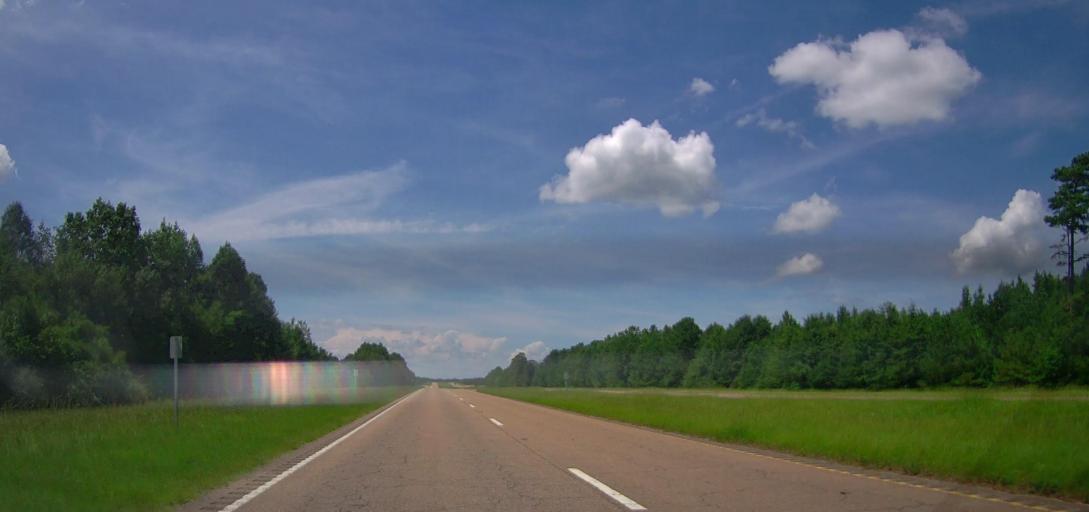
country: US
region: Mississippi
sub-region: Monroe County
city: Aberdeen
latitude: 33.8293
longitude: -88.5868
